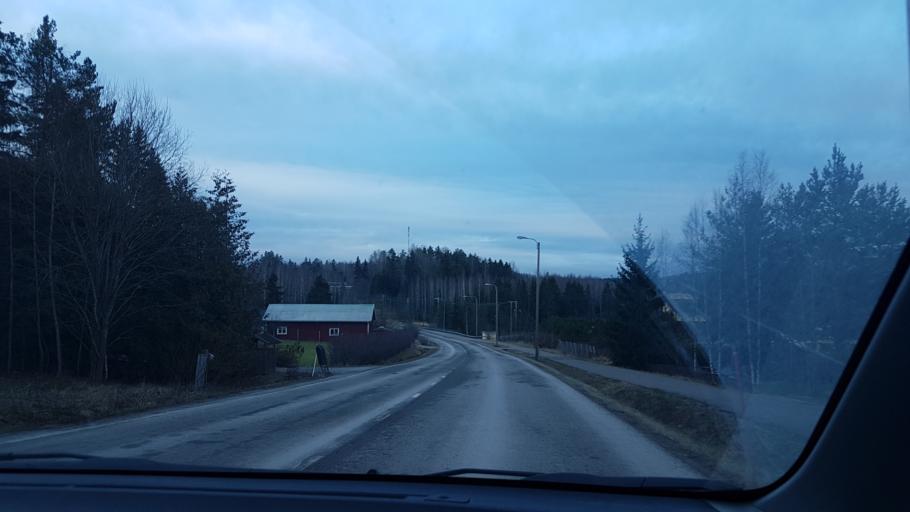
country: FI
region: Uusimaa
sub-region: Helsinki
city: Nurmijaervi
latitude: 60.3631
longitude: 24.7466
